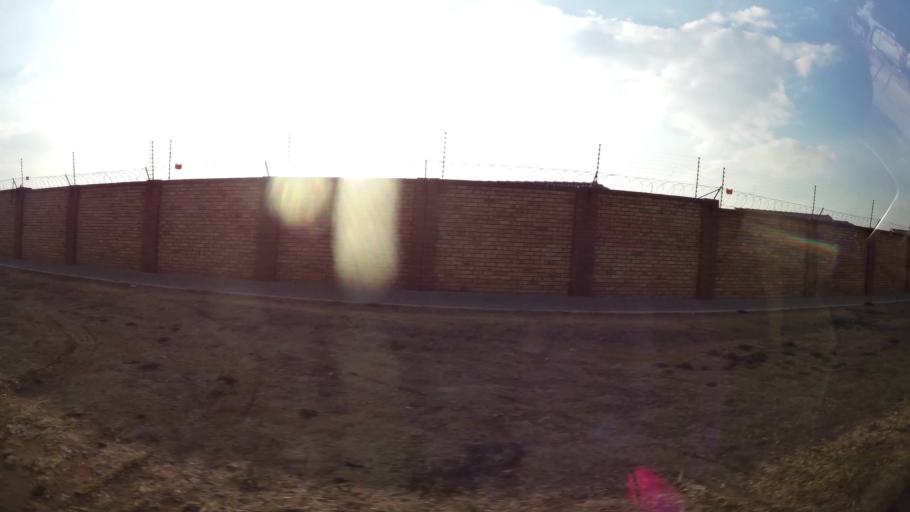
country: ZA
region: Gauteng
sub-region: Ekurhuleni Metropolitan Municipality
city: Benoni
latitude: -26.1148
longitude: 28.2872
